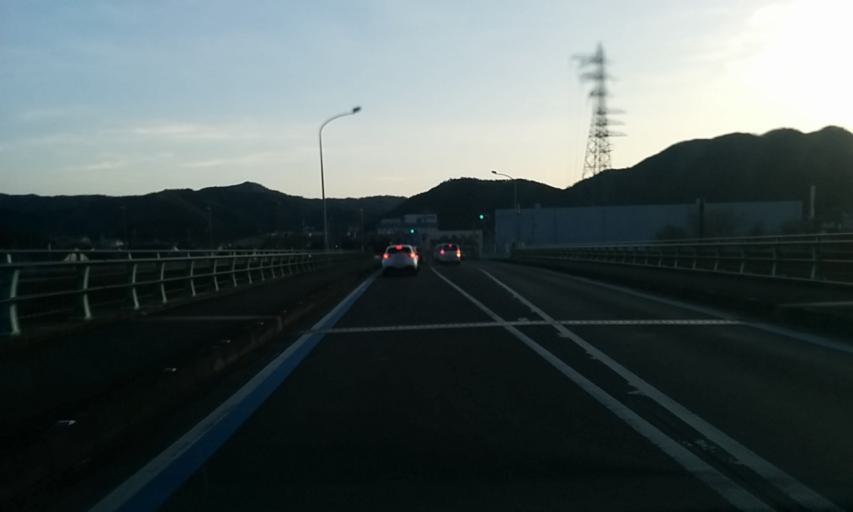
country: JP
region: Kyoto
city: Ayabe
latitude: 35.3091
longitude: 135.2587
